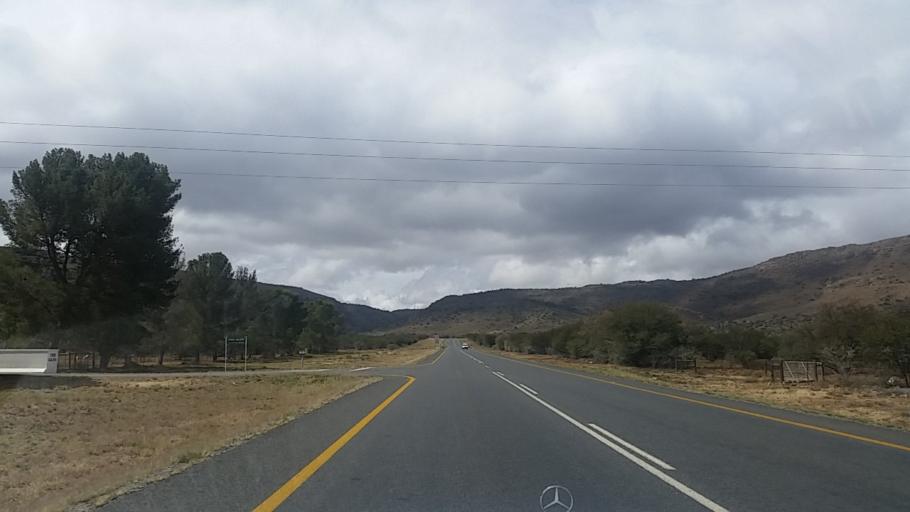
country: ZA
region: Eastern Cape
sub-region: Cacadu District Municipality
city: Graaff-Reinet
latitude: -31.9802
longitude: 24.7011
